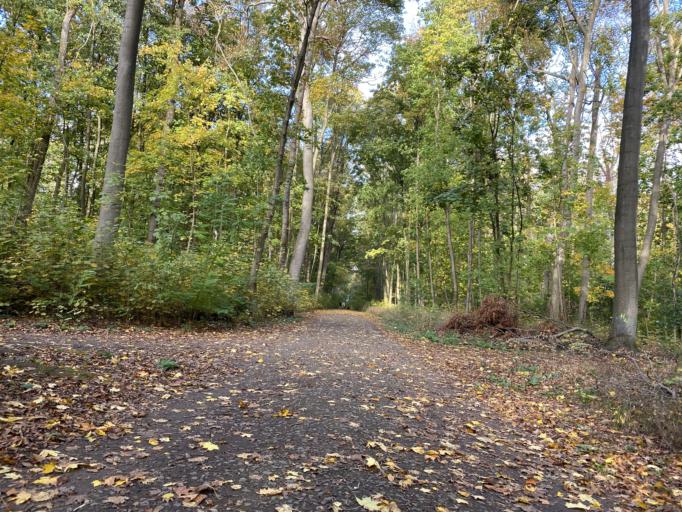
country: DE
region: Hesse
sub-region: Regierungsbezirk Darmstadt
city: Frankfurt am Main
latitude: 50.0874
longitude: 8.7128
